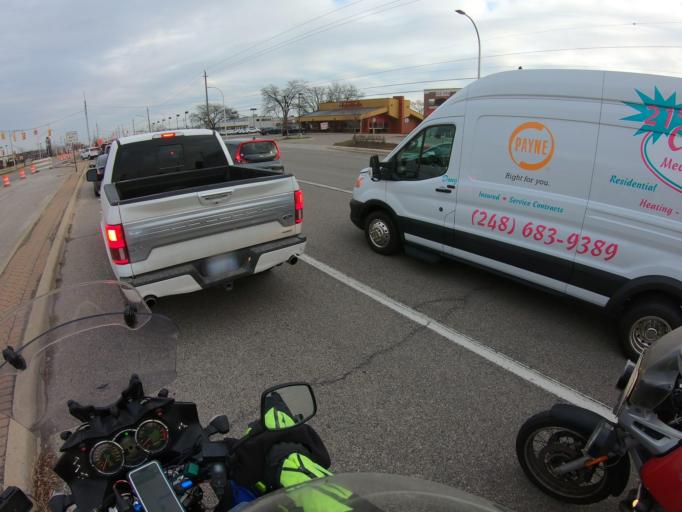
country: US
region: Michigan
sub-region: Oakland County
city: Clawson
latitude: 42.5442
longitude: -83.1053
